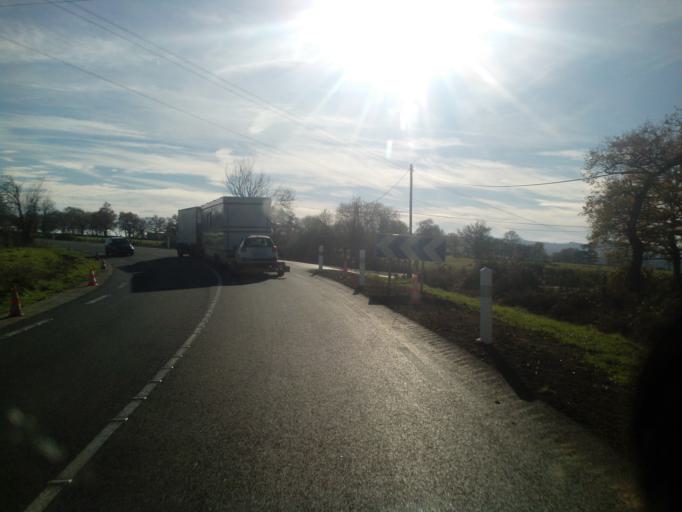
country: FR
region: Limousin
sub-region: Departement de la Haute-Vienne
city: Bellac
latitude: 46.0911
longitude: 1.0797
